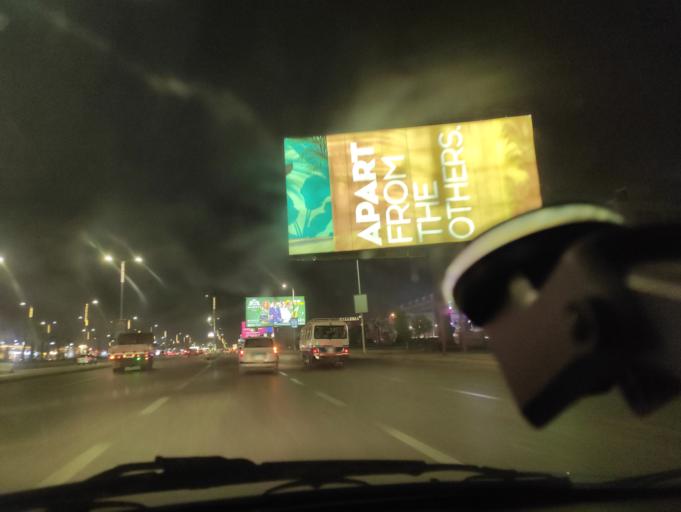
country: EG
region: Al Jizah
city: Awsim
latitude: 30.0186
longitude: 31.0064
